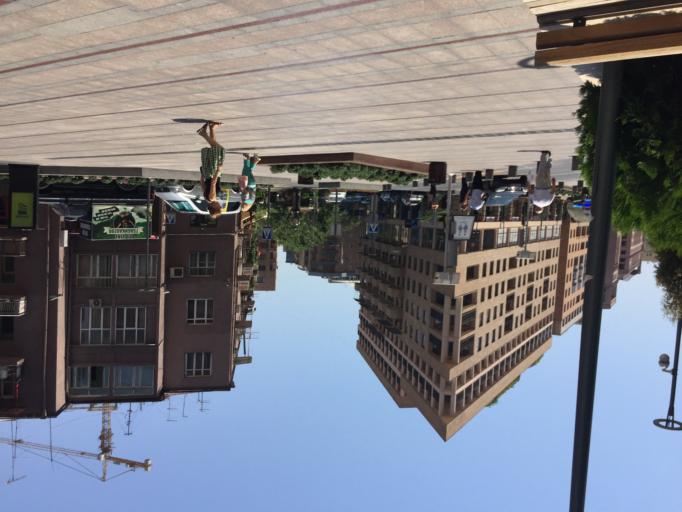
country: AM
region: Yerevan
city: Yerevan
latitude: 40.1833
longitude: 44.5149
